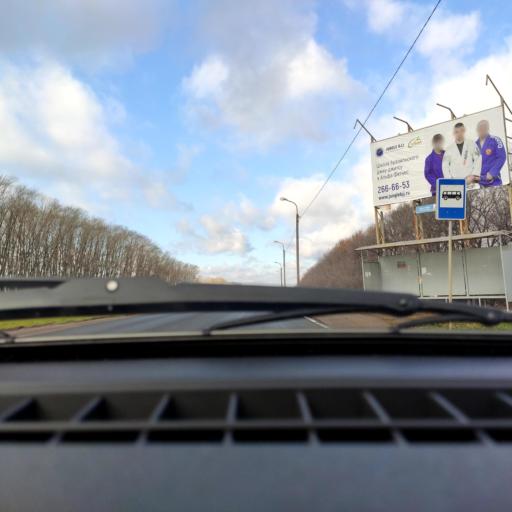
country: RU
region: Bashkortostan
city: Kabakovo
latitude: 54.6289
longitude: 56.1005
